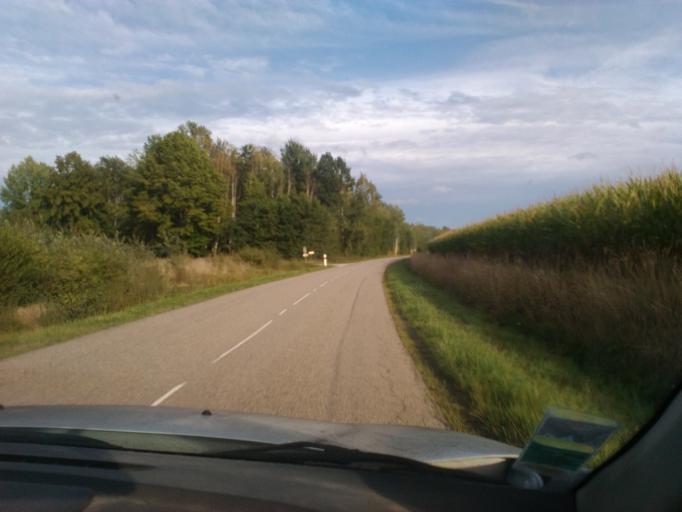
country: FR
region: Lorraine
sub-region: Departement des Vosges
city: Jeanmenil
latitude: 48.3267
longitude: 6.6804
